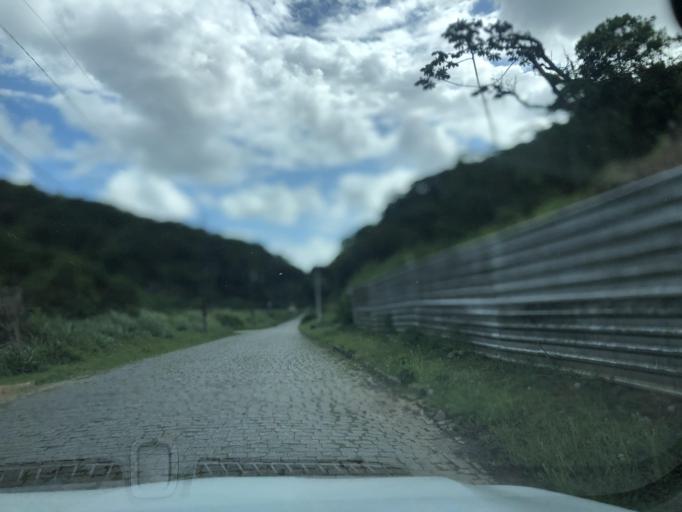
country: BR
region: Santa Catarina
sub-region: Sao Francisco Do Sul
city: Sao Francisco do Sul
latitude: -26.2336
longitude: -48.6265
